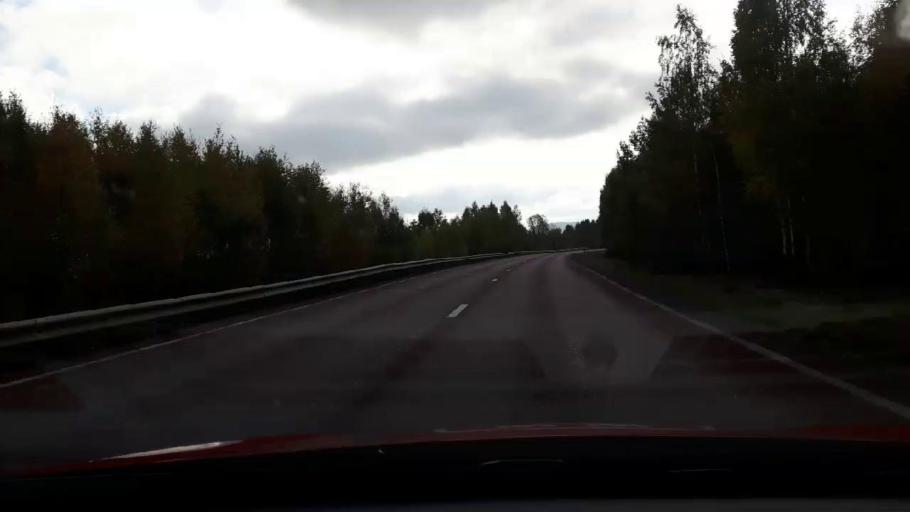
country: SE
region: Gaevleborg
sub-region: Ljusdals Kommun
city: Jaervsoe
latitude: 61.6167
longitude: 16.2941
